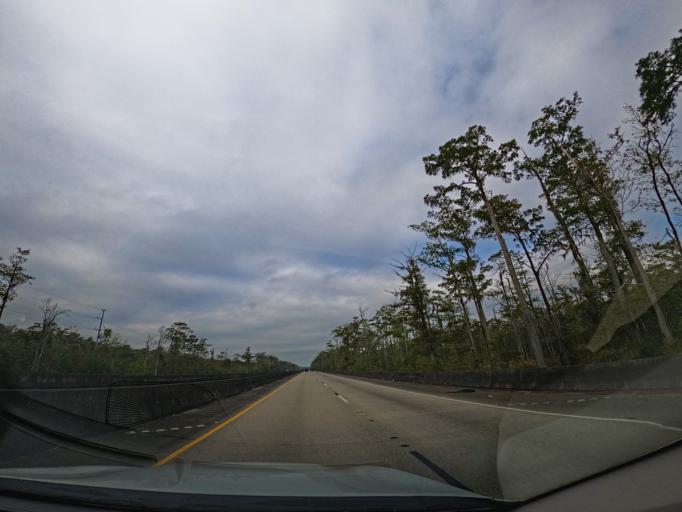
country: US
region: Louisiana
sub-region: Saint Mary Parish
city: Amelia
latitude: 29.6682
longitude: -91.0575
